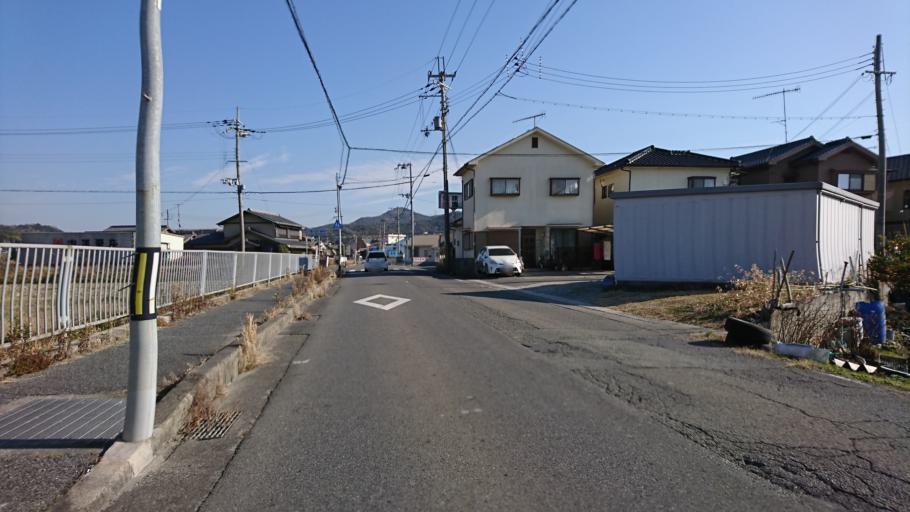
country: JP
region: Hyogo
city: Kakogawacho-honmachi
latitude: 34.8155
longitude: 134.8273
